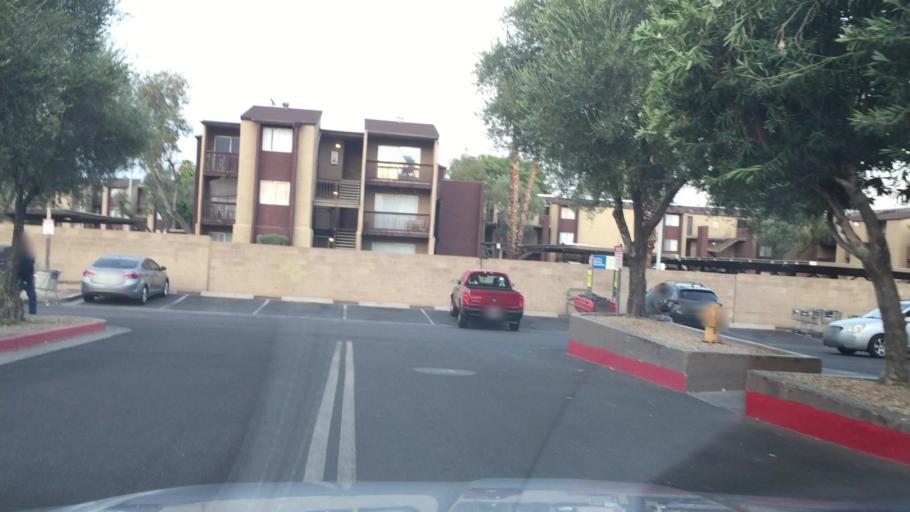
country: US
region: Arizona
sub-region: Maricopa County
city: Glendale
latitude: 33.5376
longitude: -112.0977
